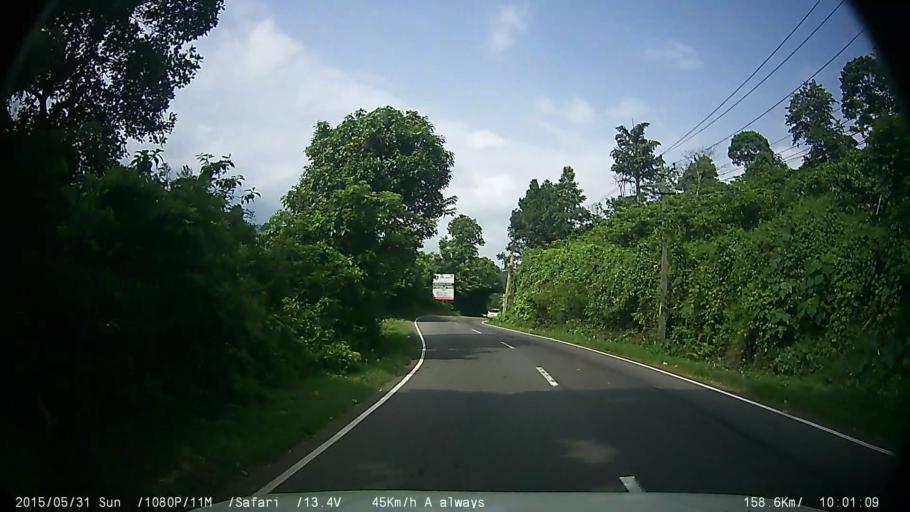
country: IN
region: Kerala
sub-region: Wayanad
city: Kalpetta
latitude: 11.5820
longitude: 76.0630
